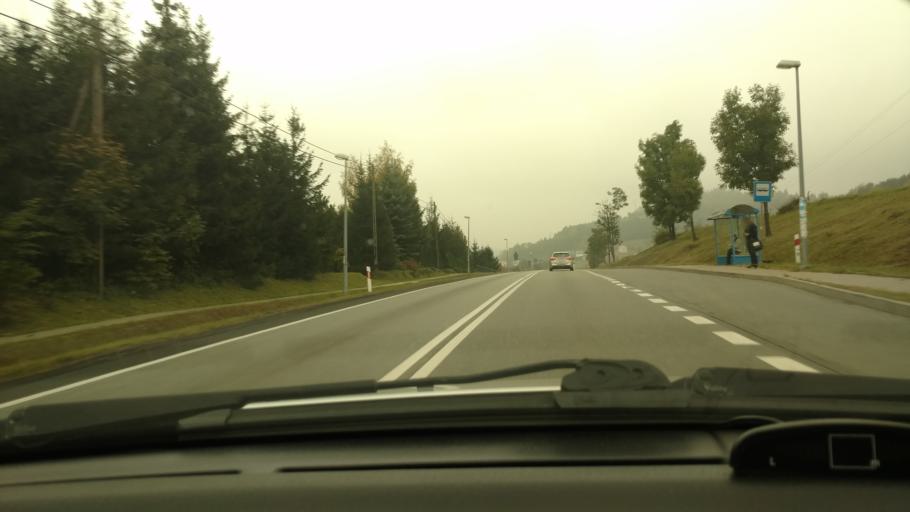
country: PL
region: Lesser Poland Voivodeship
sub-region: Powiat nowosadecki
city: Kamionka Wielka
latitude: 49.6160
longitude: 20.8452
